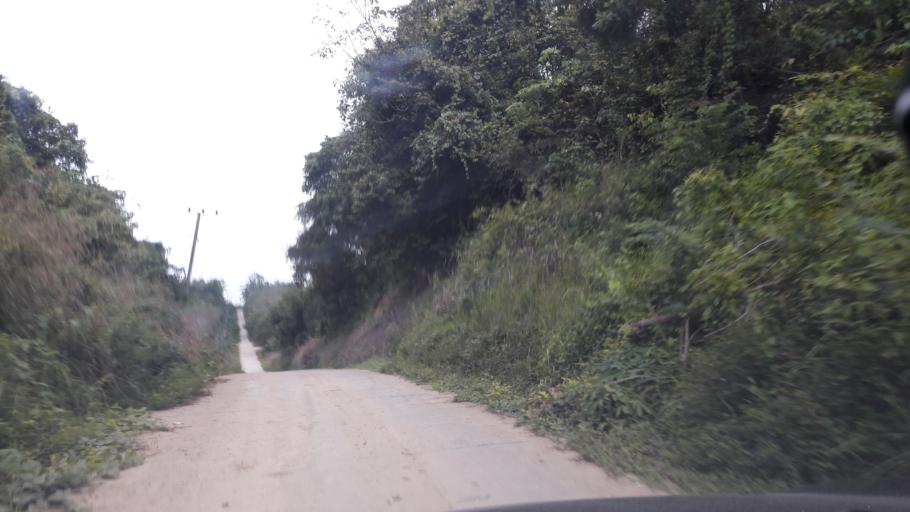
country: ID
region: South Sumatra
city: Gunungmenang
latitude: -3.1946
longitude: 103.8063
